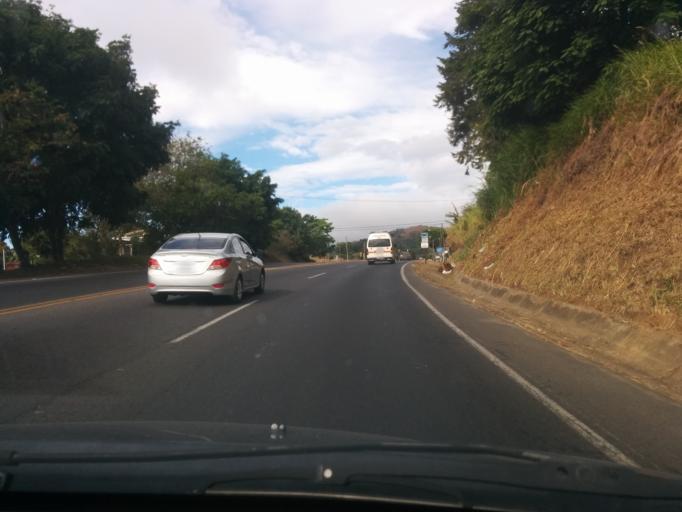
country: CR
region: Alajuela
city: San Ramon
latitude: 10.0768
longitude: -84.4677
